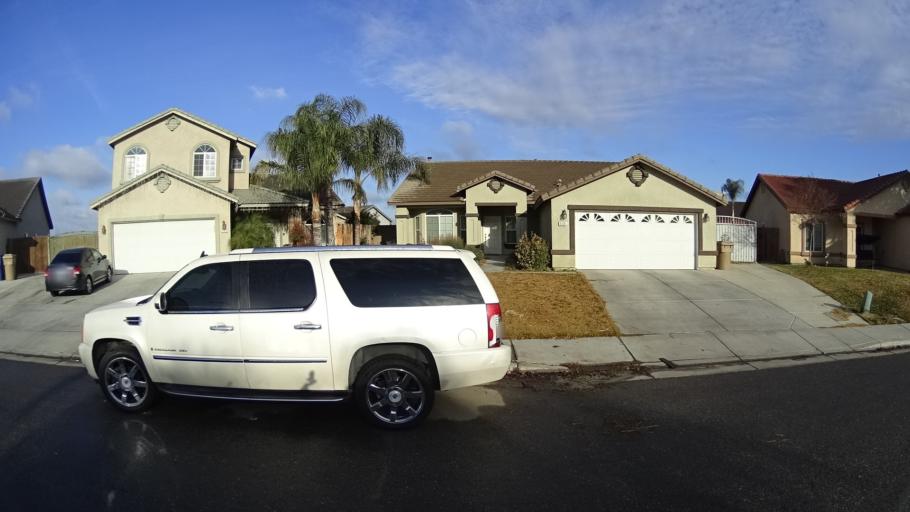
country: US
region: California
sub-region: Kern County
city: Greenfield
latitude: 35.2898
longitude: -118.9980
